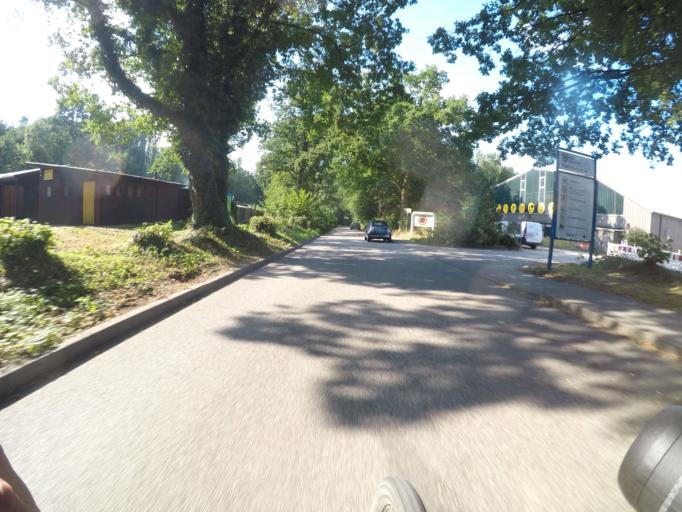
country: DE
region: Schleswig-Holstein
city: Glinde
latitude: 53.5155
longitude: 10.2078
